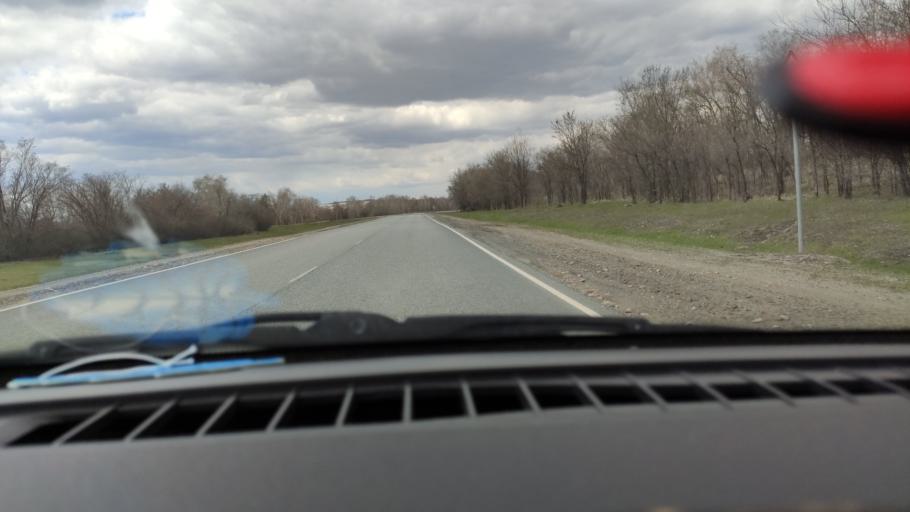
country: RU
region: Saratov
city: Tersa
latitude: 52.0825
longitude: 47.5602
